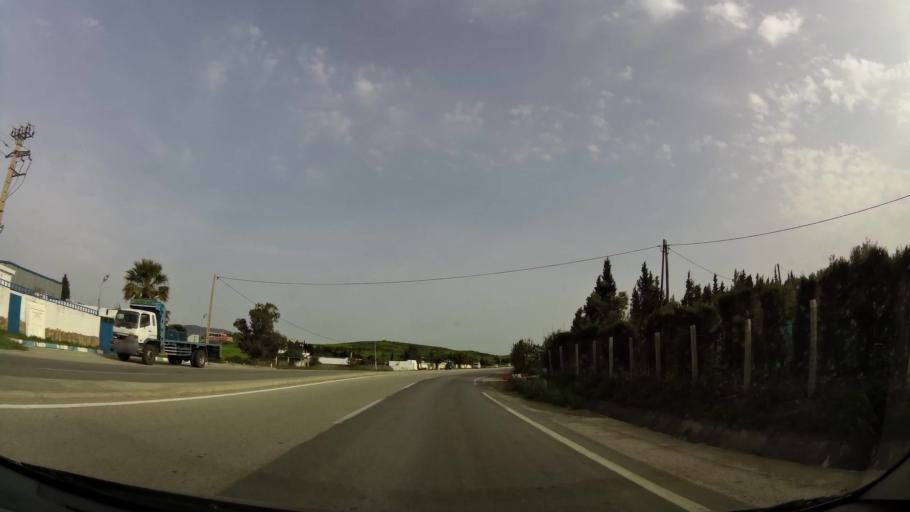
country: MA
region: Tanger-Tetouan
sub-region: Tanger-Assilah
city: Dar Chaoui
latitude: 35.6734
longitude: -5.7000
